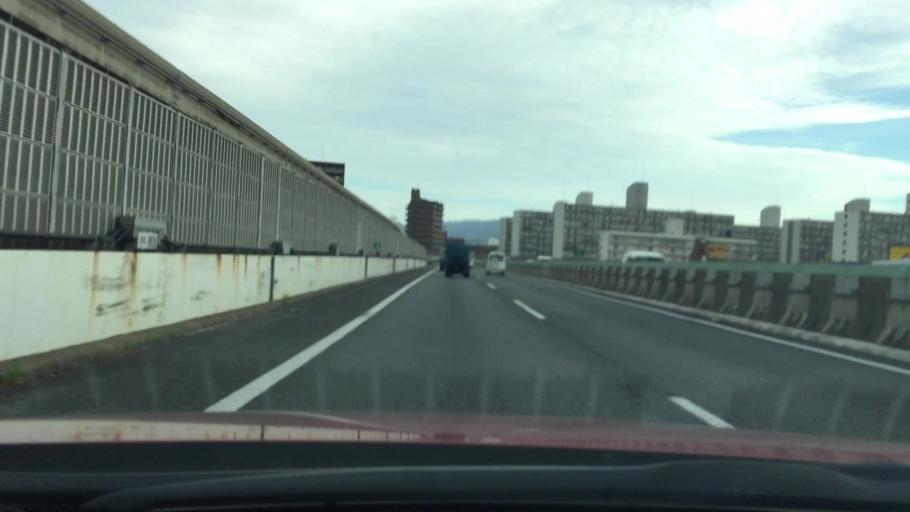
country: JP
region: Osaka
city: Ibaraki
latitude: 34.7964
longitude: 135.5663
